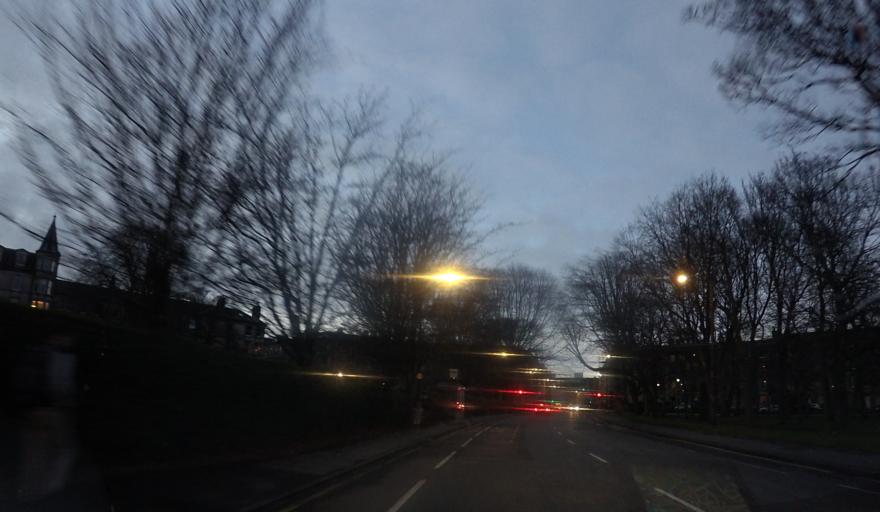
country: GB
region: Scotland
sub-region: Edinburgh
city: Edinburgh
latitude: 55.9414
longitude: -3.1996
